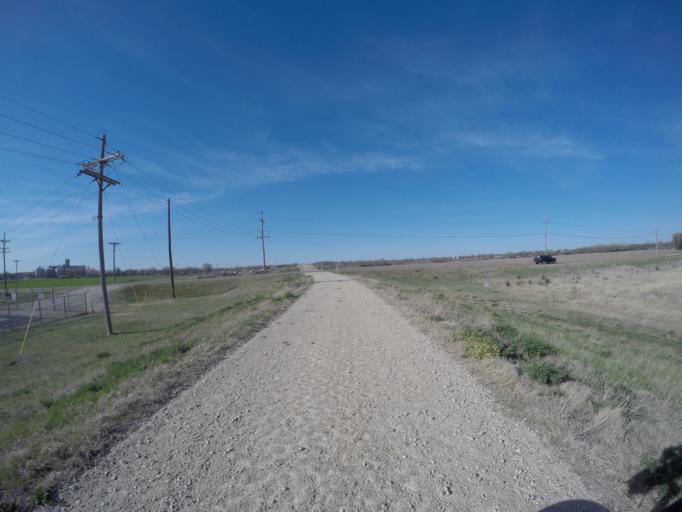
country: US
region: Kansas
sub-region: Saline County
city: Salina
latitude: 38.8485
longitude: -97.5749
